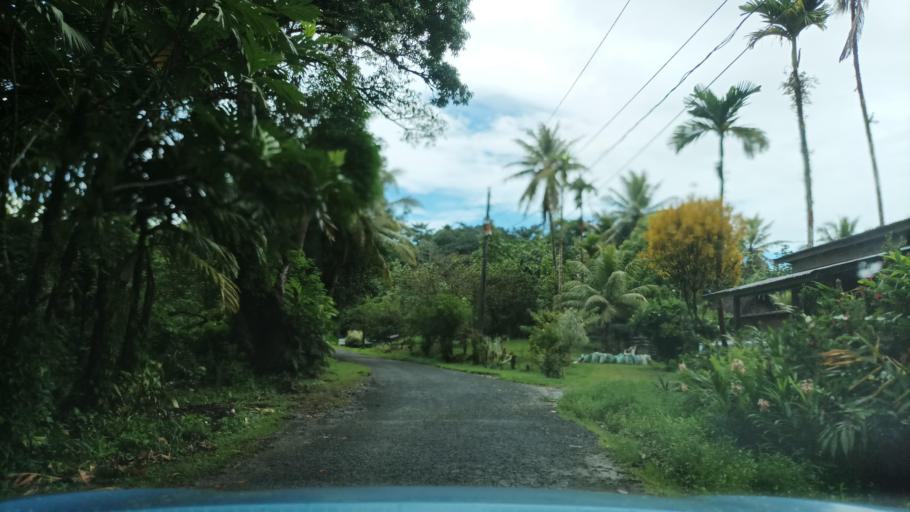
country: FM
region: Pohnpei
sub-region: Sokehs Municipality
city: Palikir - National Government Center
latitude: 6.8306
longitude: 158.1707
